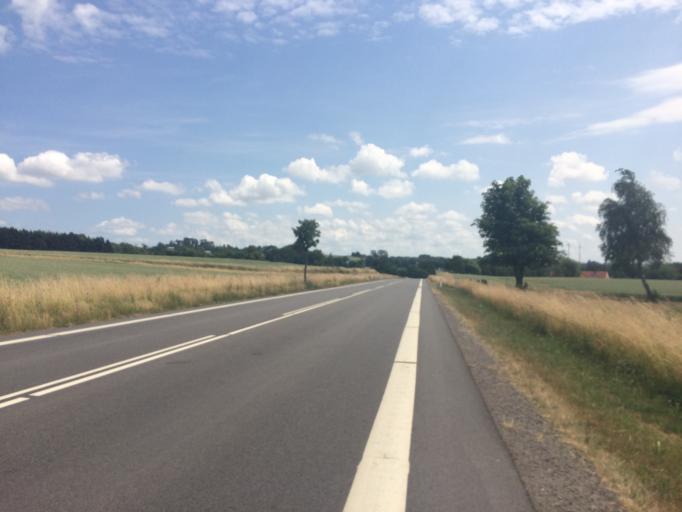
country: DK
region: Capital Region
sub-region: Bornholm Kommune
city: Ronne
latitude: 55.1789
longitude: 14.7268
